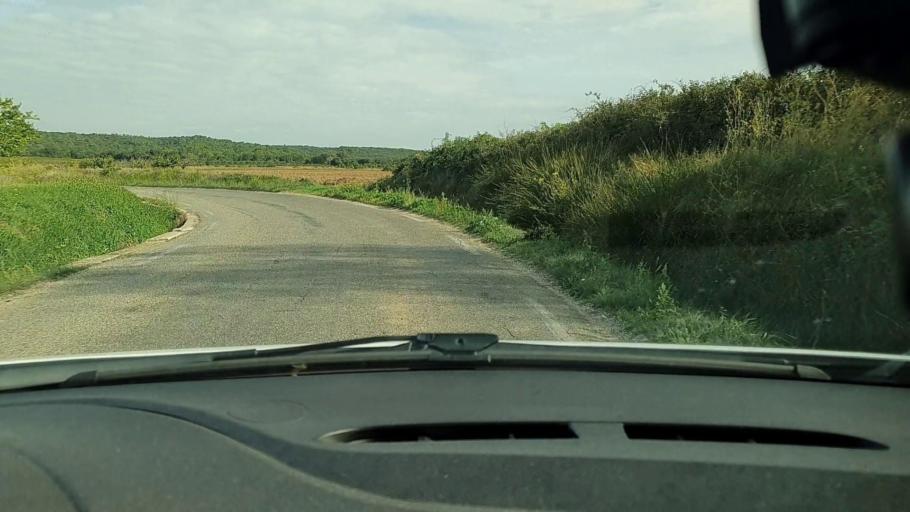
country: FR
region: Languedoc-Roussillon
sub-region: Departement du Gard
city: Saint-Quentin-la-Poterie
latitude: 44.0578
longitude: 4.4386
